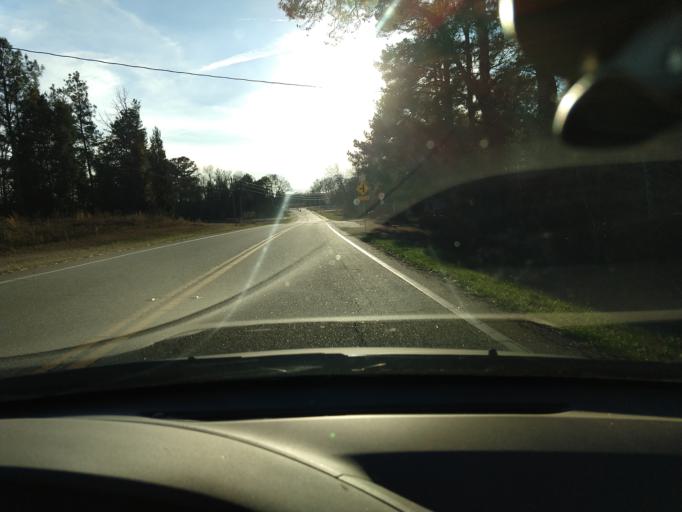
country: US
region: Georgia
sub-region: Sumter County
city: Americus
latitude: 32.1201
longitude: -84.1619
